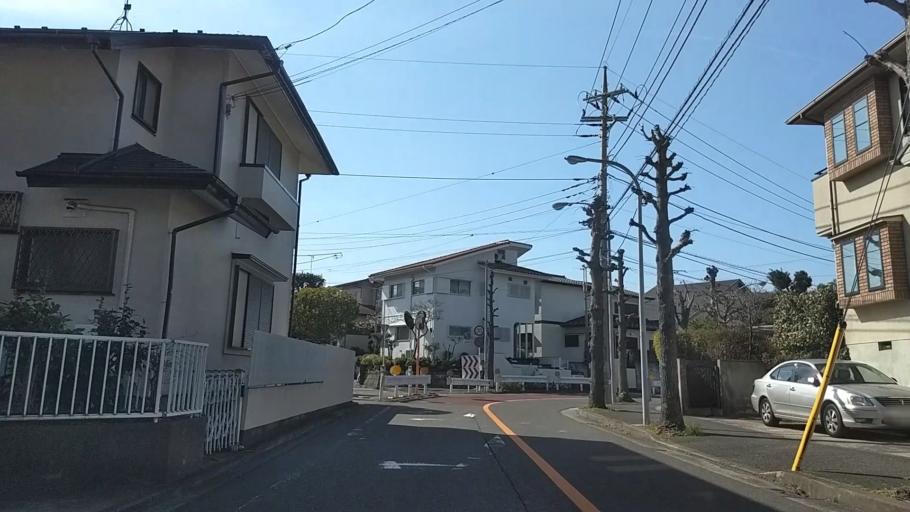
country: JP
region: Kanagawa
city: Kamakura
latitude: 35.3753
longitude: 139.5495
